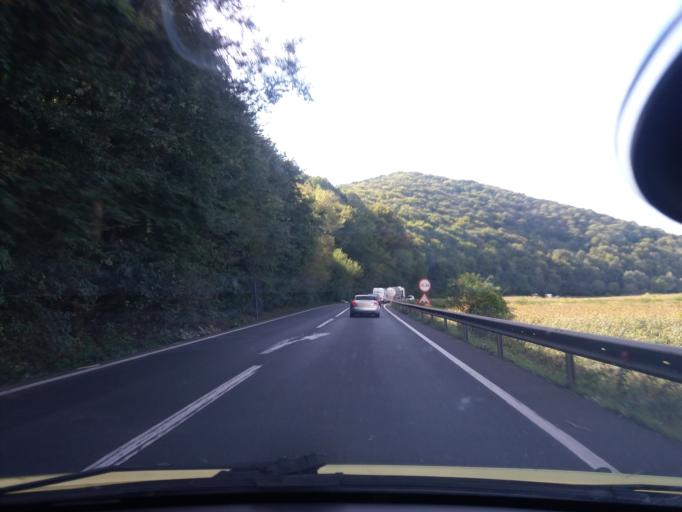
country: RO
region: Hunedoara
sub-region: Comuna Ilia
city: Ilia
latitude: 45.9202
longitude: 22.7081
